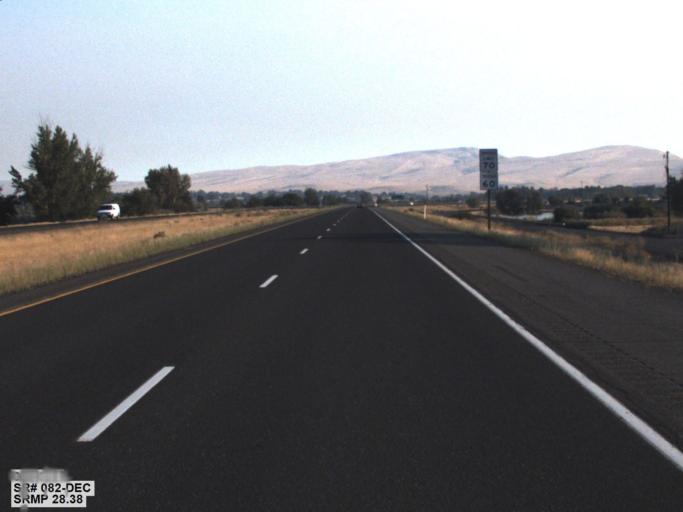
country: US
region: Washington
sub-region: Yakima County
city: Selah
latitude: 46.6545
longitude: -120.4966
